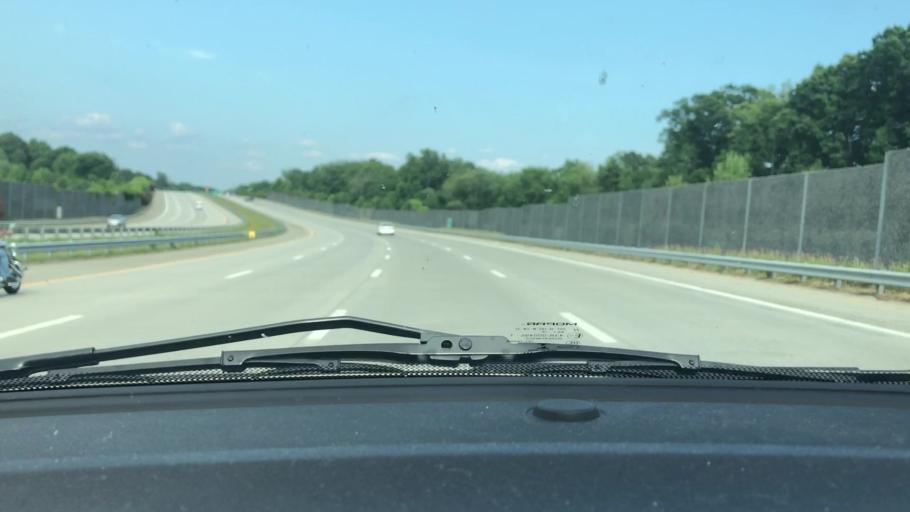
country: US
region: North Carolina
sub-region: Guilford County
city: Jamestown
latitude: 36.0199
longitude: -79.8726
